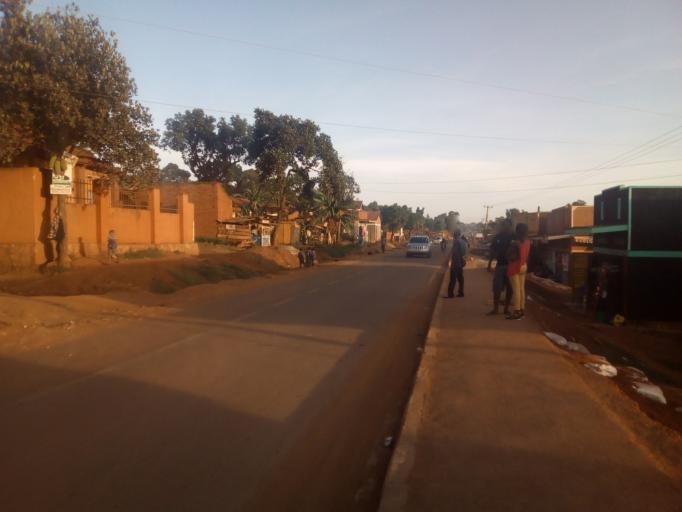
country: UG
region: Central Region
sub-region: Wakiso District
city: Kajansi
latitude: 0.2468
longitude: 32.5714
